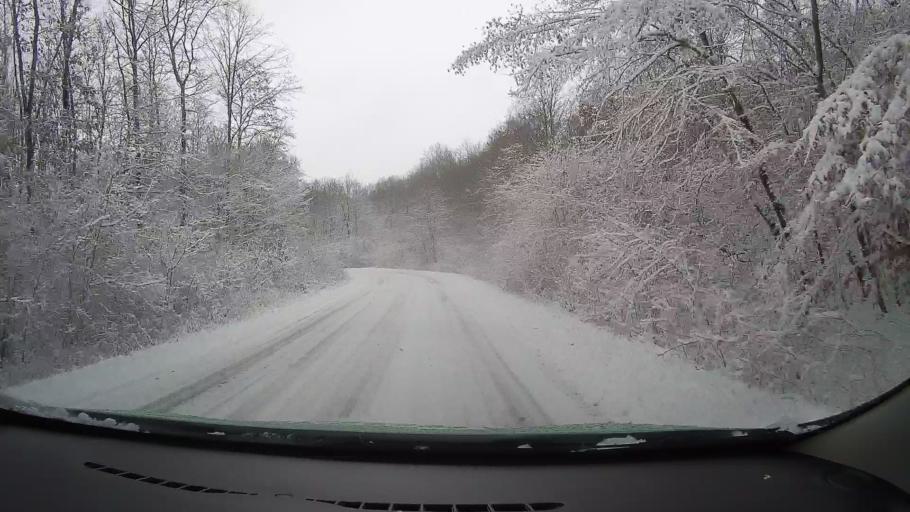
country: RO
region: Hunedoara
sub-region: Comuna Pestisu Mic
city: Pestisu Mic
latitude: 45.8109
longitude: 22.9044
